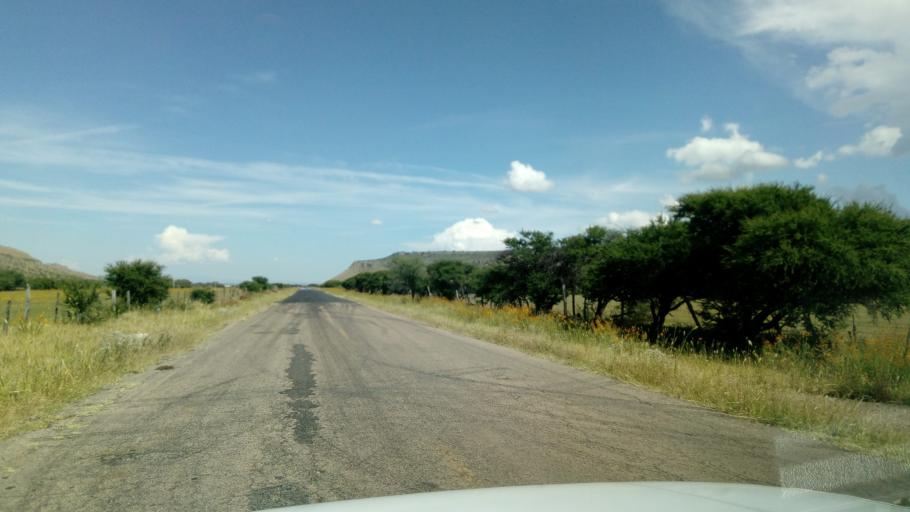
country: MX
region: Durango
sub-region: Durango
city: Jose Refugio Salcido
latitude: 23.8030
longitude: -104.4844
